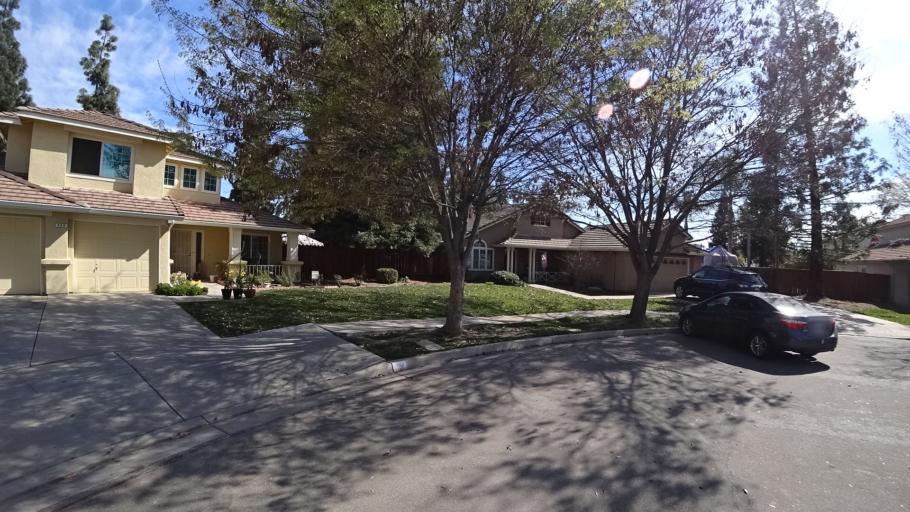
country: US
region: California
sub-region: Fresno County
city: Clovis
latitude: 36.8531
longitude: -119.7664
